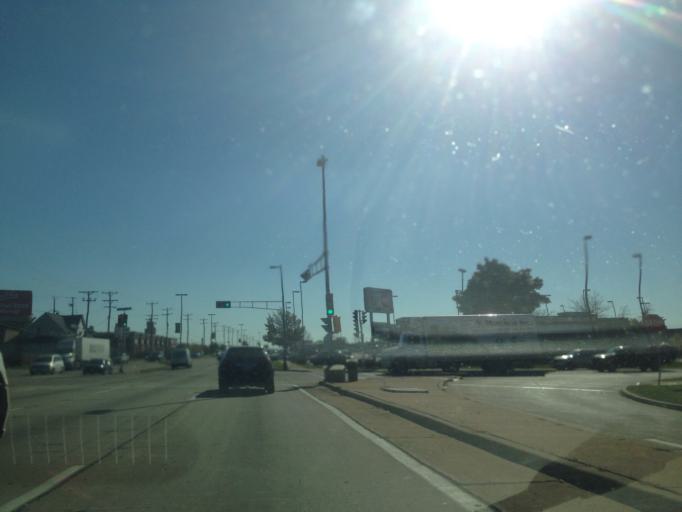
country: US
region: Wisconsin
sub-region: Milwaukee County
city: West Milwaukee
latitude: 43.0174
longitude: -87.9679
